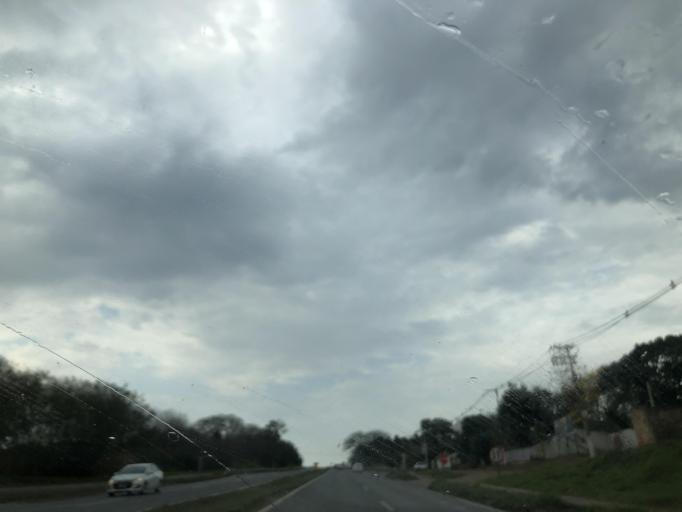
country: BR
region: Sao Paulo
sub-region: Salto De Pirapora
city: Salto de Pirapora
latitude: -23.6351
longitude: -47.5706
